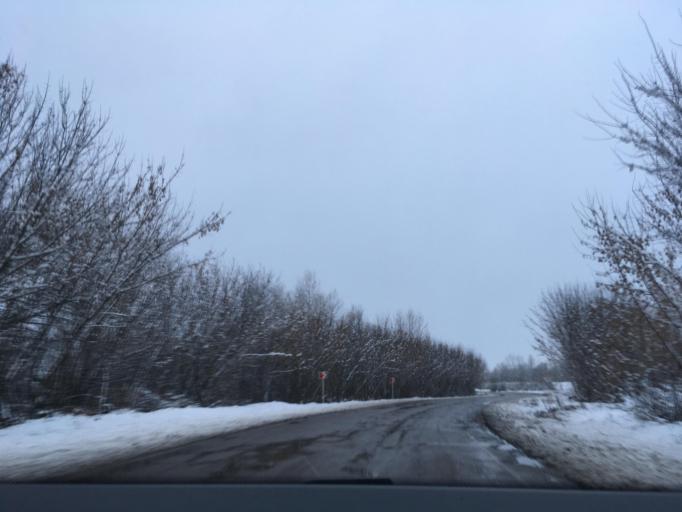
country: RU
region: Voronezj
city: Mitrofanovka
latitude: 50.1293
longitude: 39.9956
